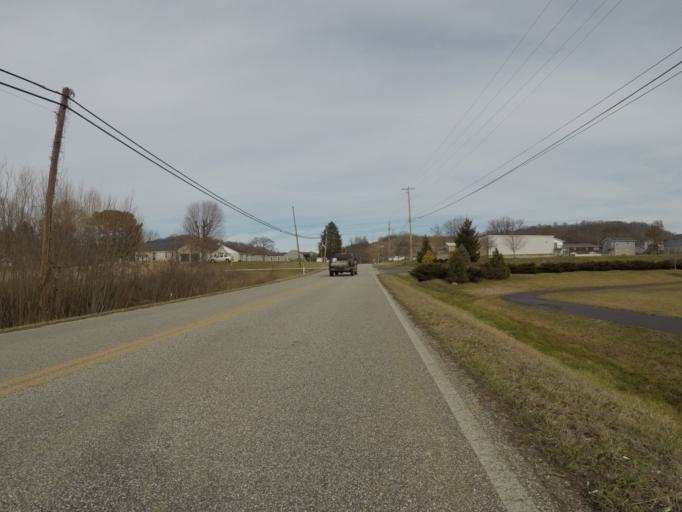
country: US
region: West Virginia
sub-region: Cabell County
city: Pea Ridge
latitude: 38.4449
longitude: -82.3763
